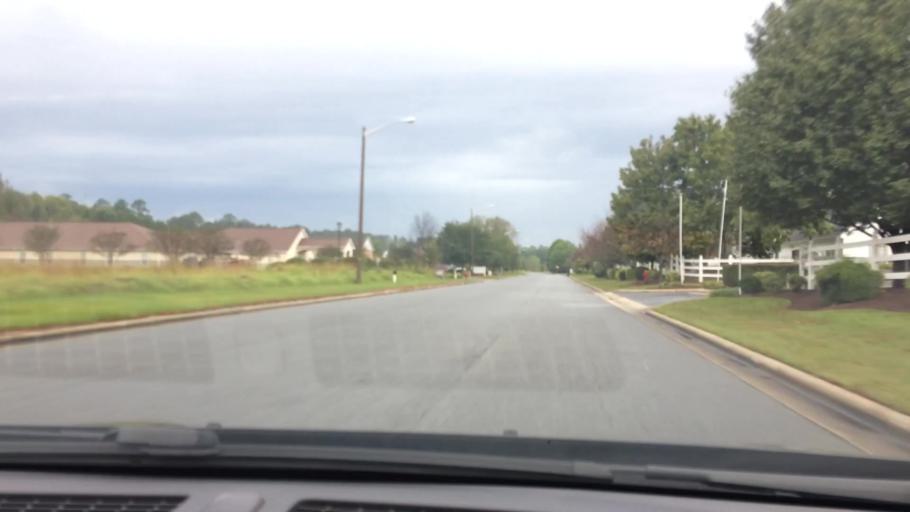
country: US
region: North Carolina
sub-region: Pitt County
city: Windsor
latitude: 35.5653
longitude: -77.3632
